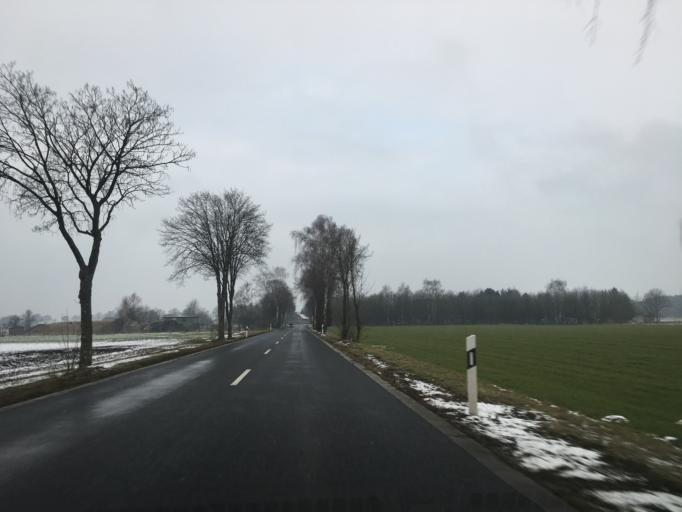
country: DE
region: North Rhine-Westphalia
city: Wegberg
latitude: 51.1353
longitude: 6.2292
